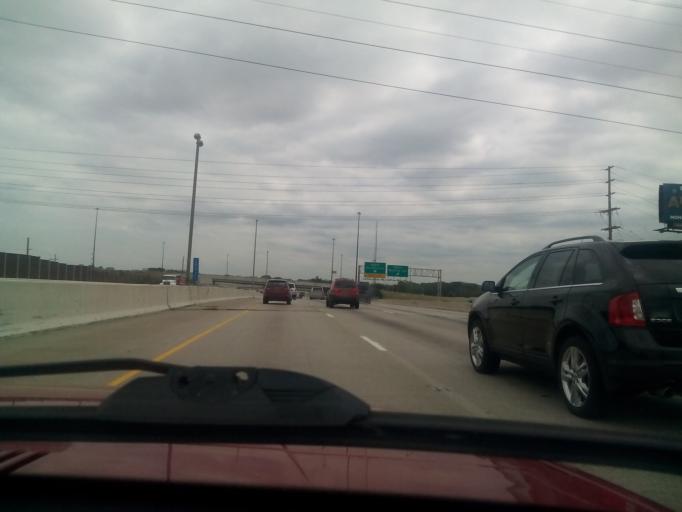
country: US
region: Indiana
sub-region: Lake County
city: Highland
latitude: 41.5741
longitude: -87.4667
